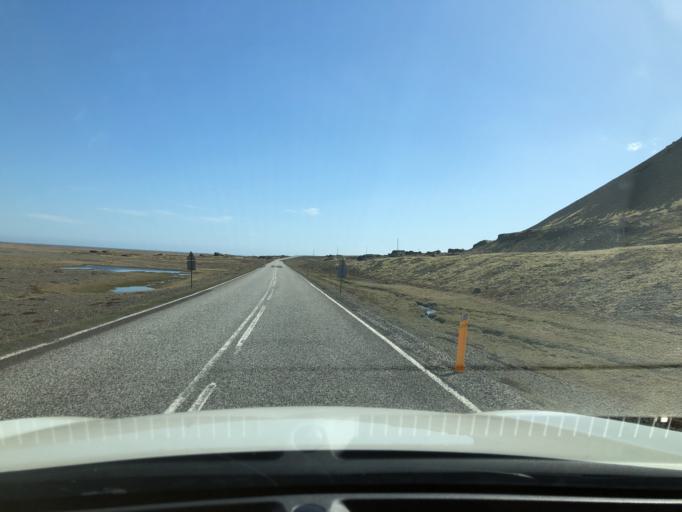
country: IS
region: East
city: Hoefn
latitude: 64.3802
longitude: -14.9321
